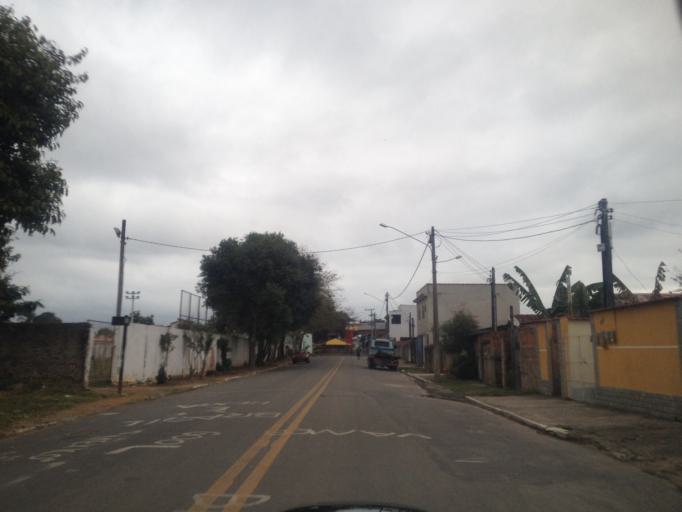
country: BR
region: Rio de Janeiro
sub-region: Porto Real
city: Porto Real
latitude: -22.4090
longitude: -44.2969
